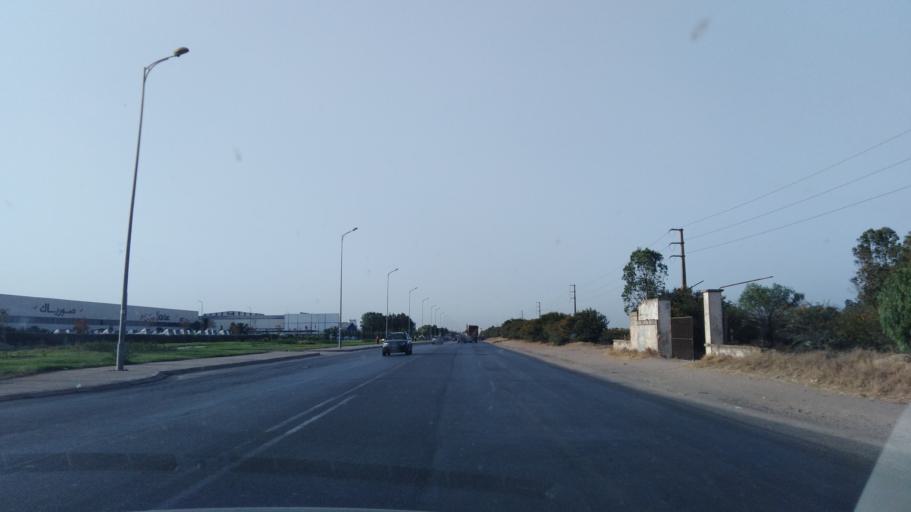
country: MA
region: Chaouia-Ouardigha
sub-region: Settat Province
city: Berrechid
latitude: 33.2475
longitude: -7.5856
